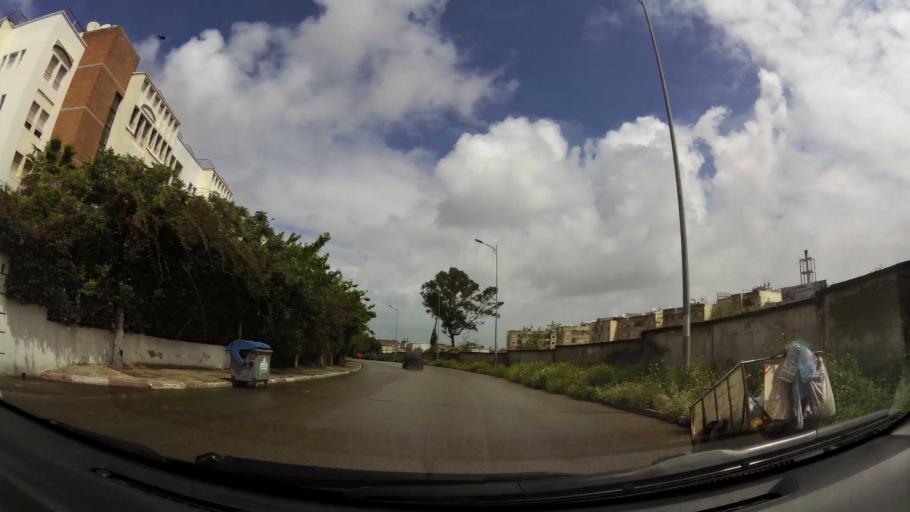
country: MA
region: Grand Casablanca
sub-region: Casablanca
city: Casablanca
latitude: 33.5584
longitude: -7.6730
